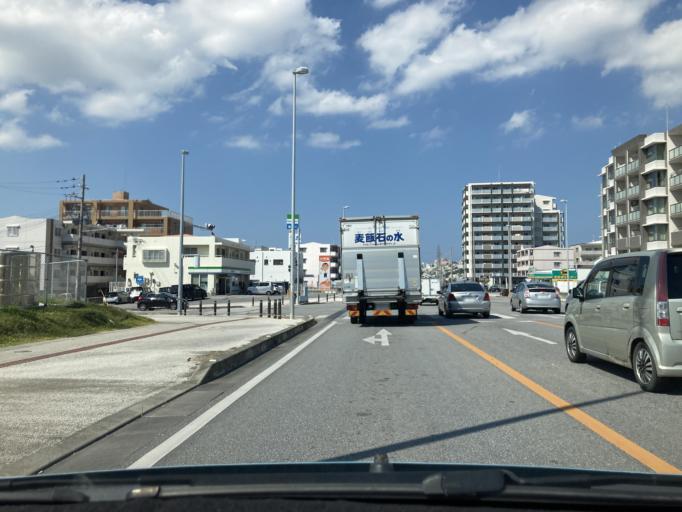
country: JP
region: Okinawa
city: Tomigusuku
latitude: 26.1900
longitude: 127.7163
